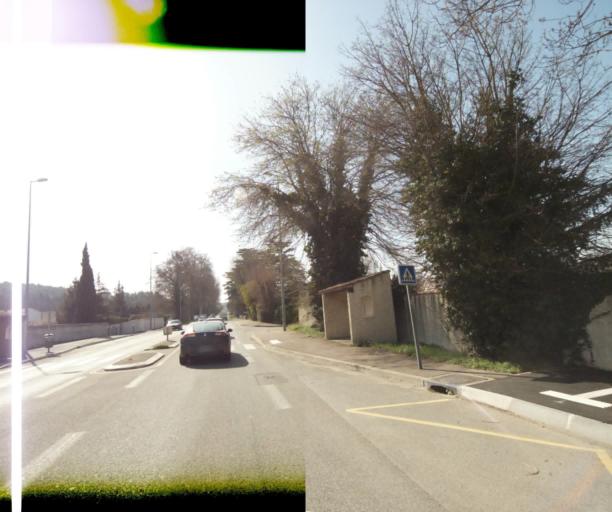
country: FR
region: Provence-Alpes-Cote d'Azur
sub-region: Departement des Bouches-du-Rhone
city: Bouc-Bel-Air
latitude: 43.4573
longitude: 5.4035
